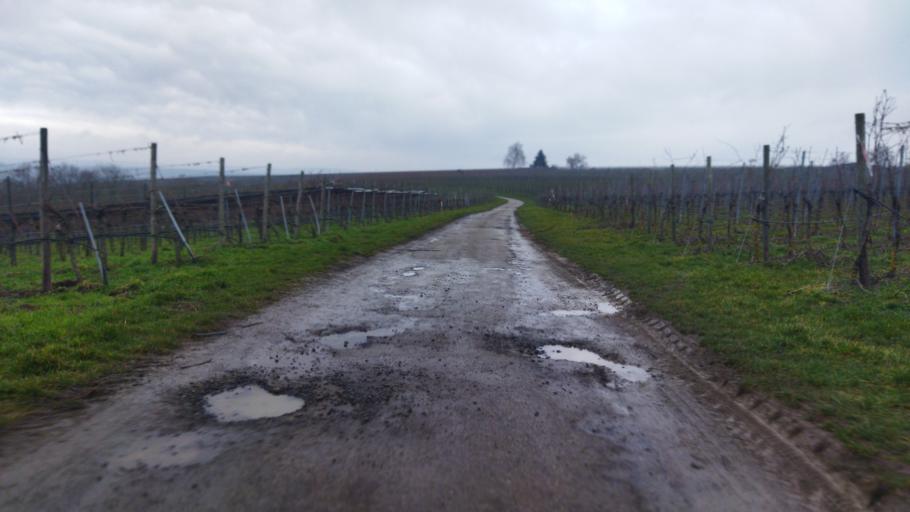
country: DE
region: Baden-Wuerttemberg
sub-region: Regierungsbezirk Stuttgart
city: Neckarwestheim
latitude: 49.0585
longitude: 9.1889
